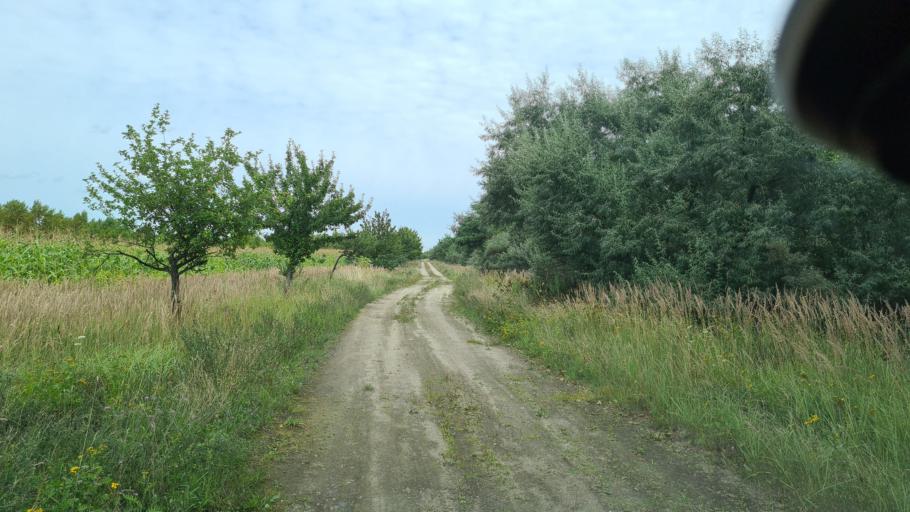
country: DE
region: Brandenburg
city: Spremberg
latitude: 51.5769
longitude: 14.3007
